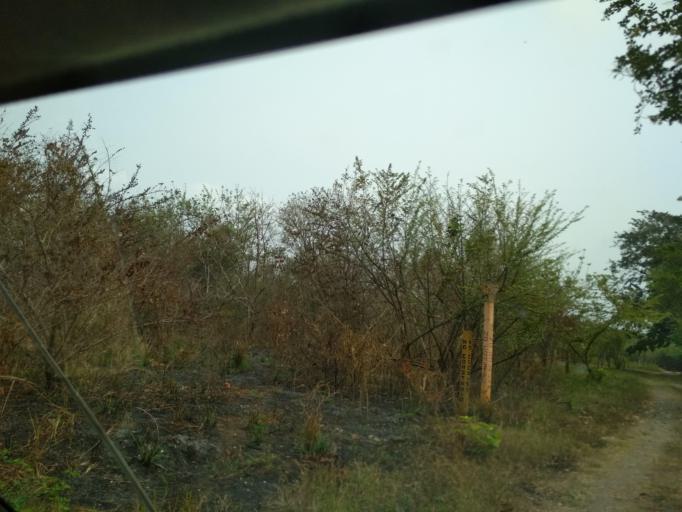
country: MX
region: Veracruz
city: Paso del Toro
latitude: 19.0230
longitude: -96.1416
